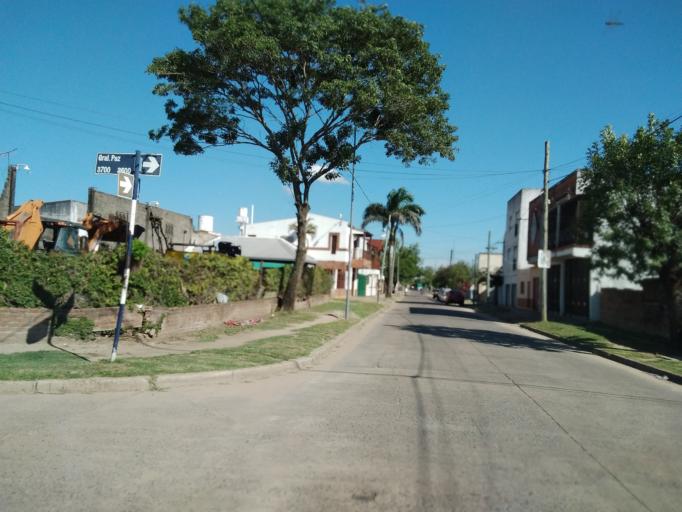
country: AR
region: Corrientes
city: Corrientes
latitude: -27.4821
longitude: -58.8080
